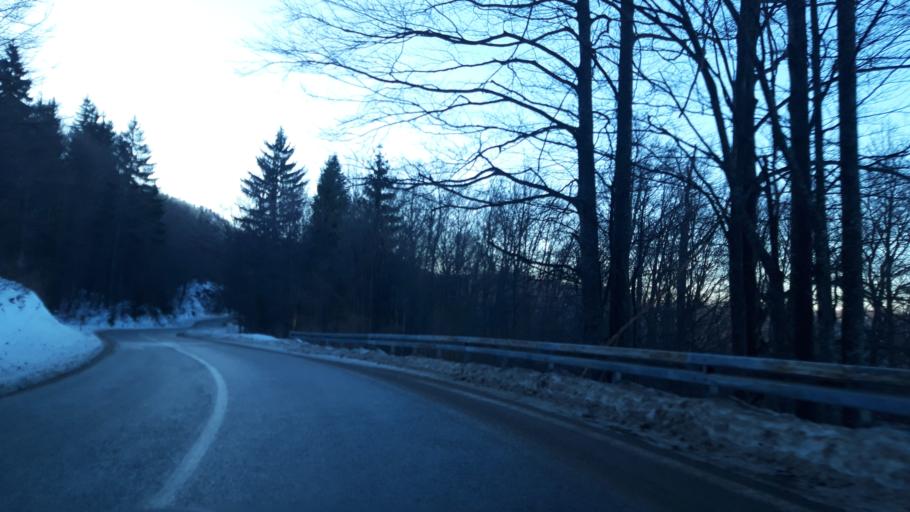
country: BA
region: Republika Srpska
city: Vlasenica
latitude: 44.1574
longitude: 18.9383
